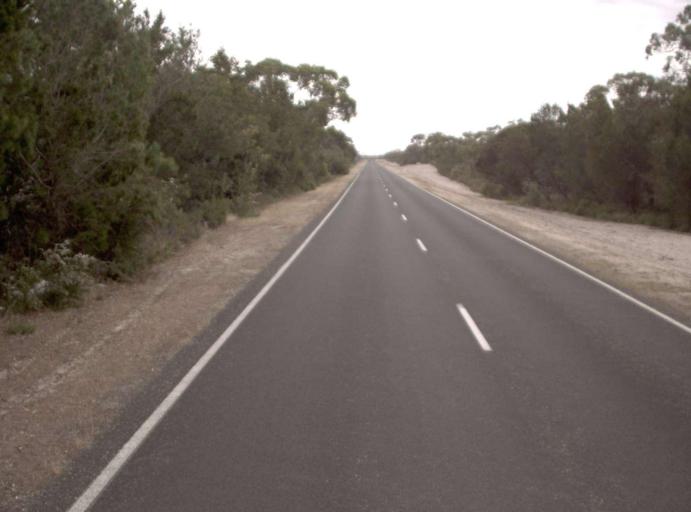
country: AU
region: Victoria
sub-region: Wellington
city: Sale
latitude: -38.1785
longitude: 147.3791
